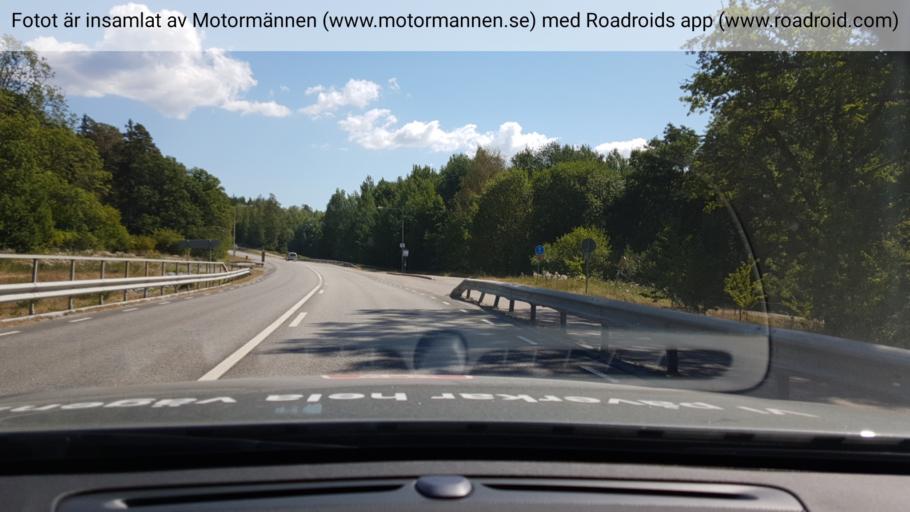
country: SE
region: Stockholm
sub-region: Ekero Kommun
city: Ekeroe
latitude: 59.3030
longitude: 17.7854
